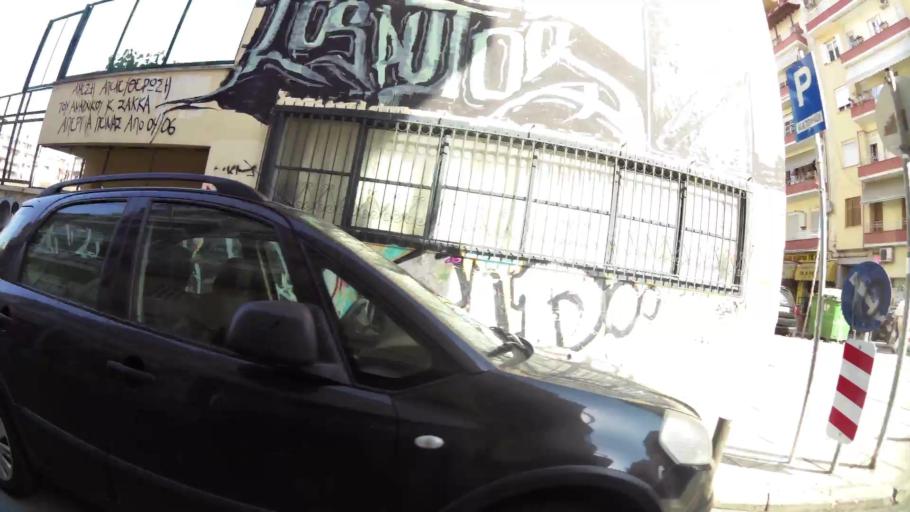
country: GR
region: Central Macedonia
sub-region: Nomos Thessalonikis
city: Agios Pavlos
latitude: 40.6367
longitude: 22.9489
